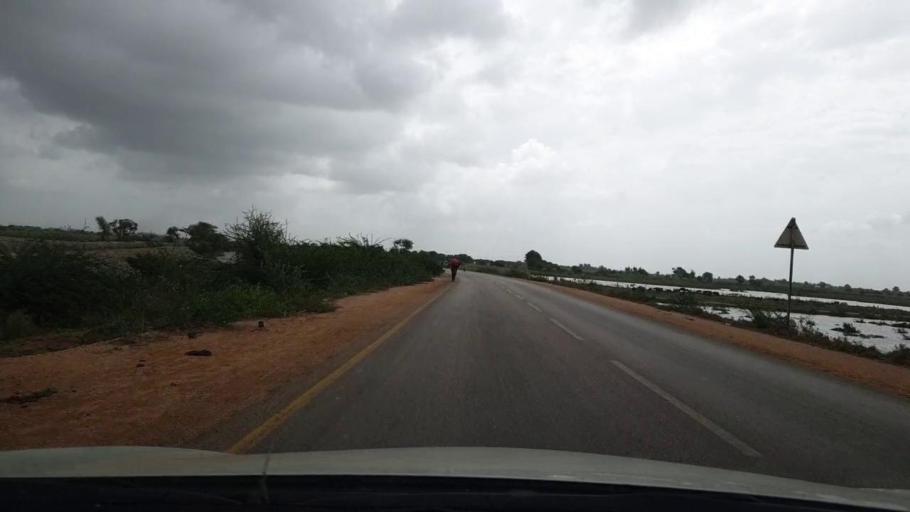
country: PK
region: Sindh
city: Mirpur Batoro
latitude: 24.6019
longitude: 68.2350
